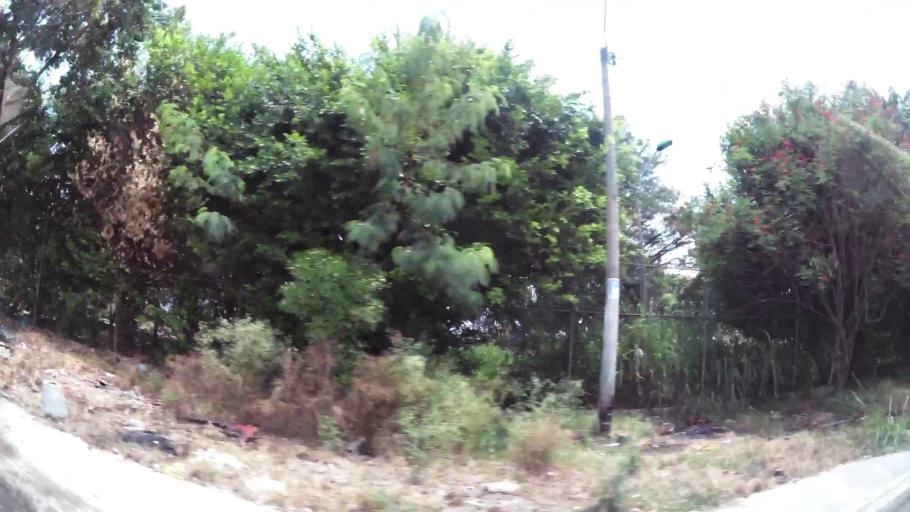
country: CO
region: Valle del Cauca
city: Cali
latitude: 3.4660
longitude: -76.4804
